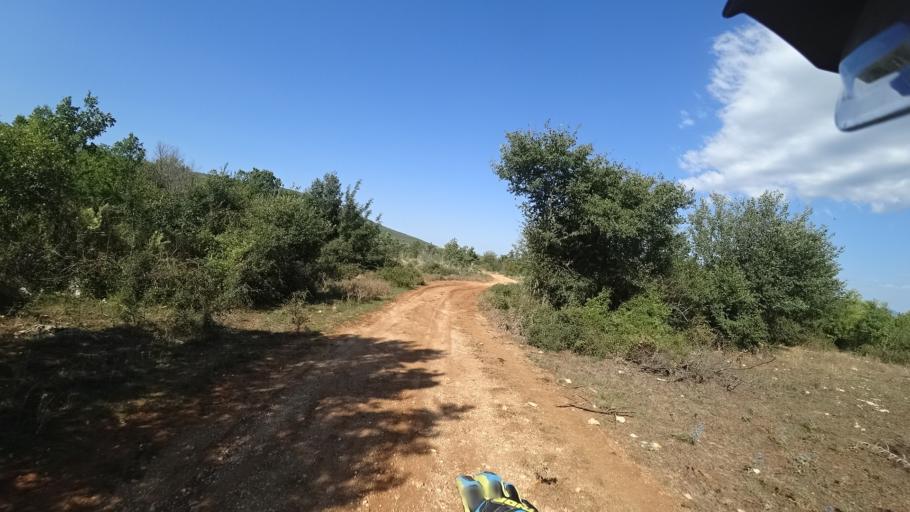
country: HR
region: Sibensko-Kniniska
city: Knin
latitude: 43.9711
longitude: 16.1807
